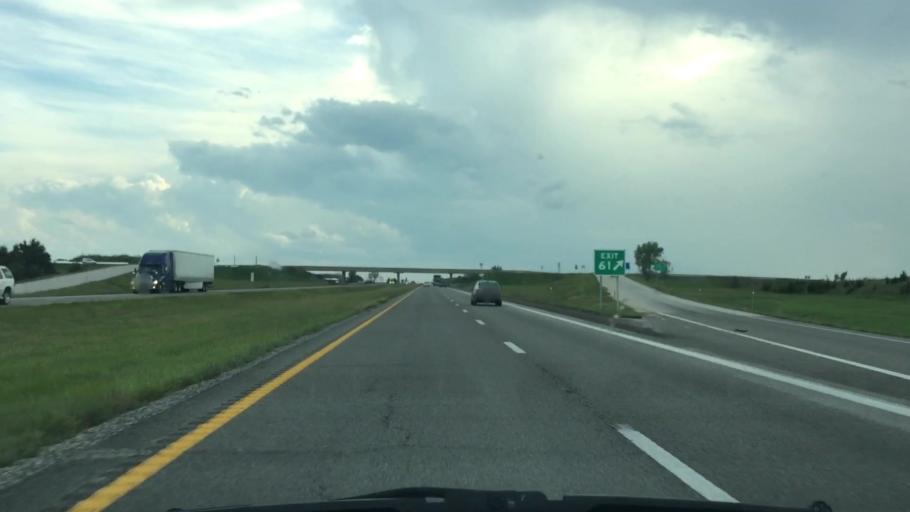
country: US
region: Missouri
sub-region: Clinton County
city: Cameron
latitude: 39.8564
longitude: -94.1757
